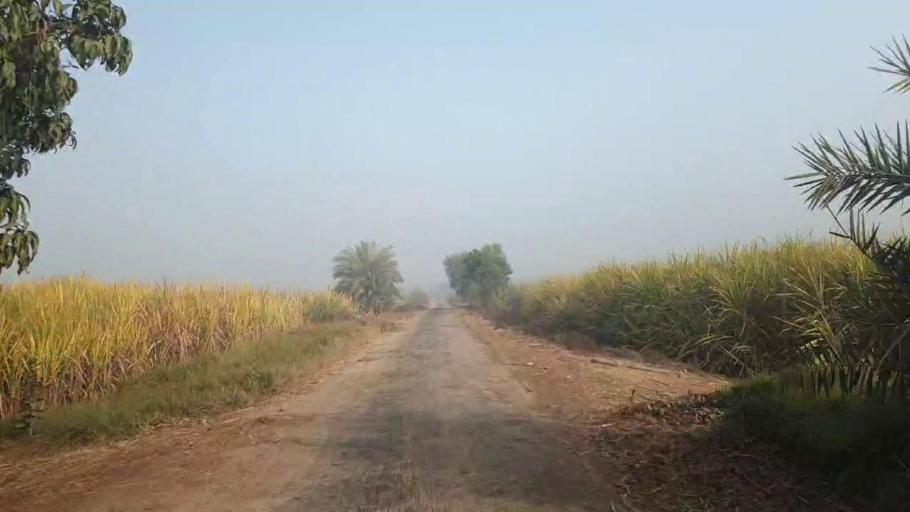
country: PK
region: Sindh
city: Tando Adam
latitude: 25.7967
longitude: 68.6334
